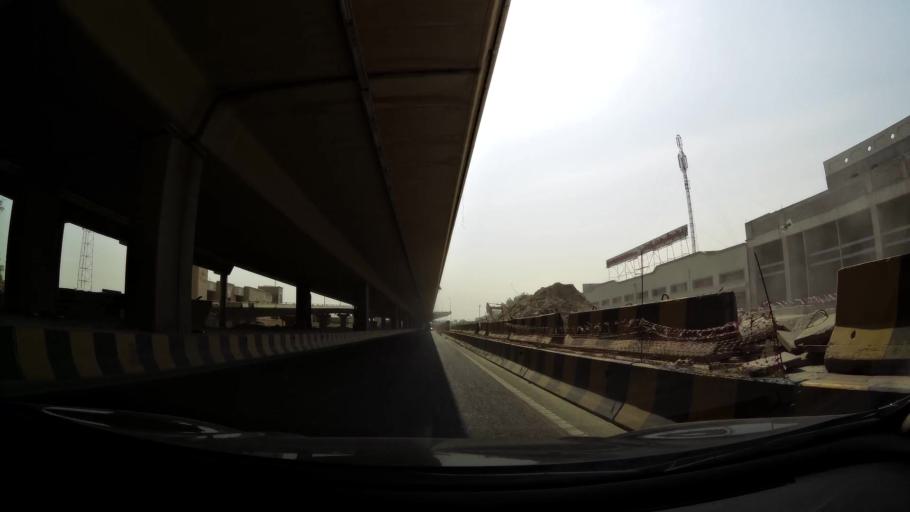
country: KW
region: Al Asimah
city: Ar Rabiyah
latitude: 29.3279
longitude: 47.9331
